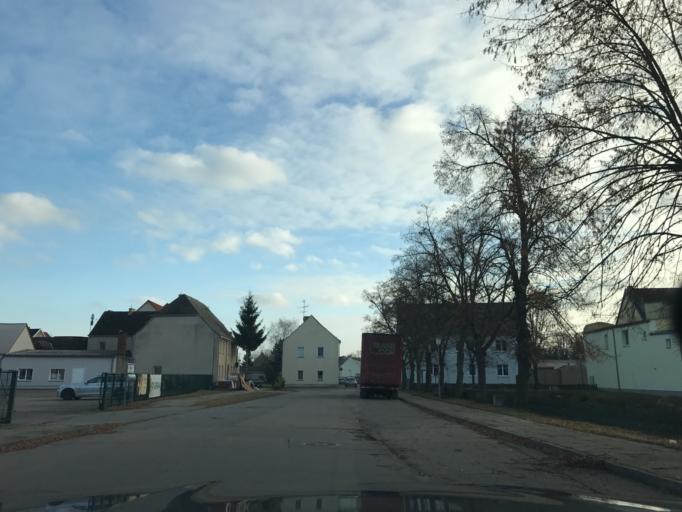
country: DE
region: Brandenburg
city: Ziesar
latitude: 52.2681
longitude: 12.2939
